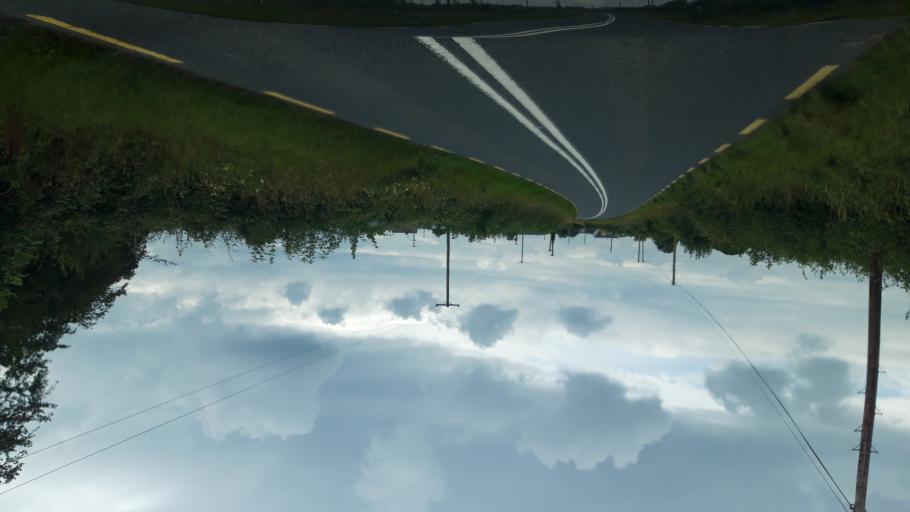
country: IE
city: Ballylinan
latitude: 52.9258
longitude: -7.0614
